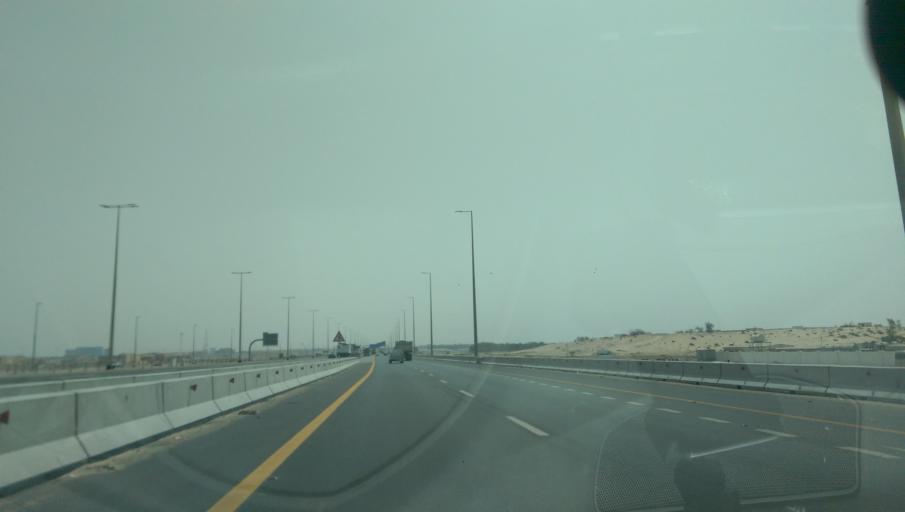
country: AE
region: Abu Dhabi
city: Abu Dhabi
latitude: 24.2977
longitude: 54.5823
